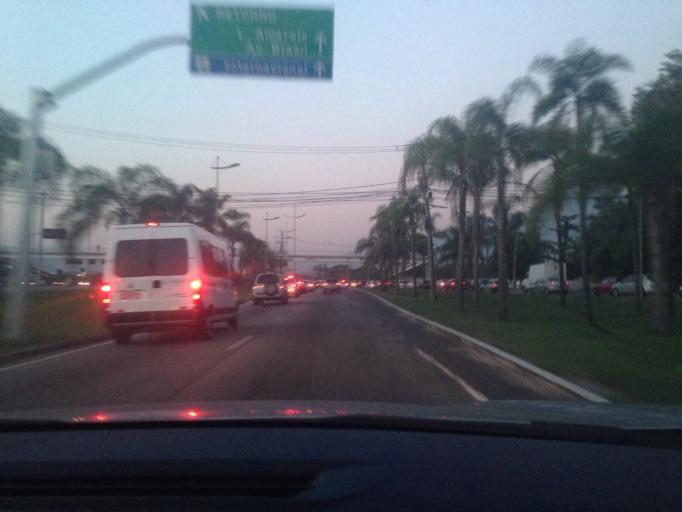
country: BR
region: Rio de Janeiro
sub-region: Sao Joao De Meriti
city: Sao Joao de Meriti
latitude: -22.9718
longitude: -43.3617
